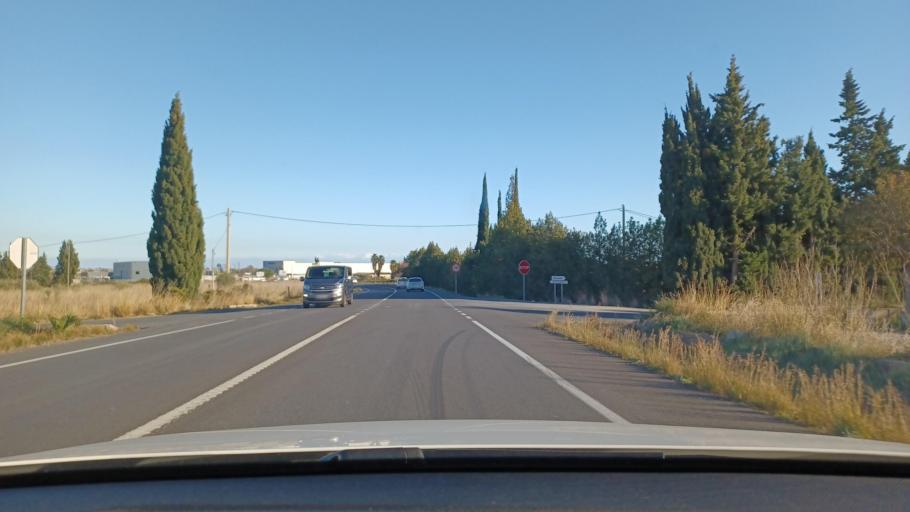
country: ES
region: Catalonia
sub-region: Provincia de Tarragona
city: Amposta
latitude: 40.6970
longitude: 0.5748
